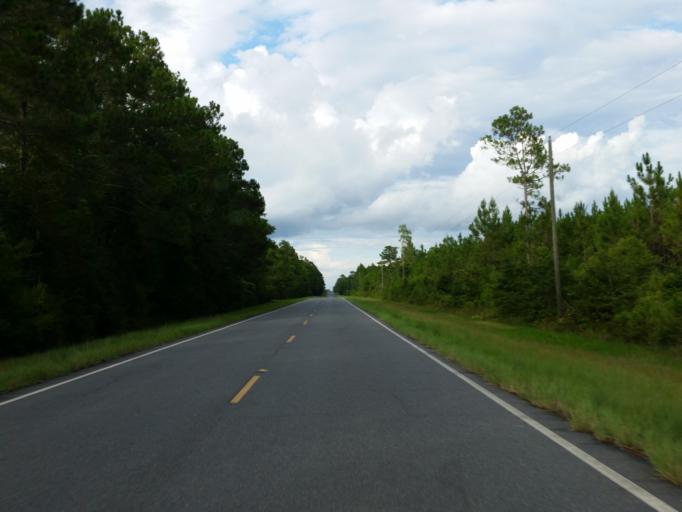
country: US
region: Florida
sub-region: Hamilton County
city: Jasper
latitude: 30.6028
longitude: -82.6593
